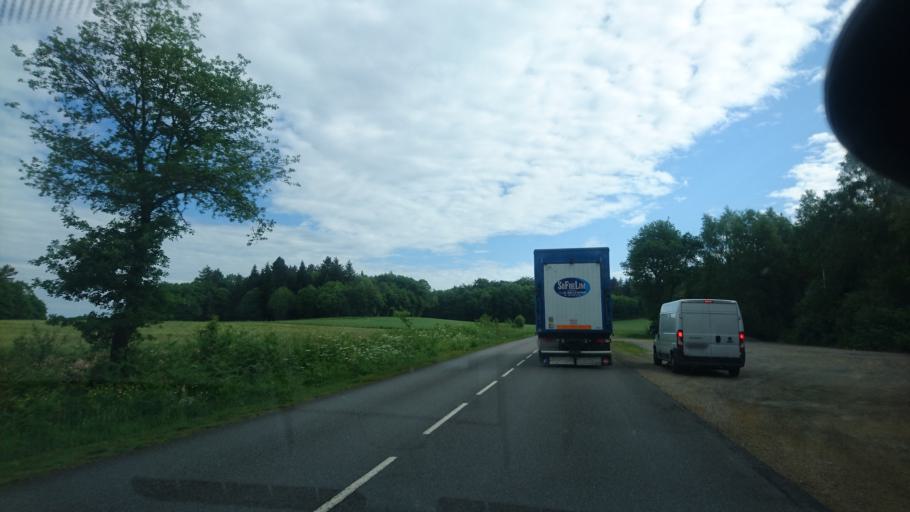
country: FR
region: Limousin
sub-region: Departement de la Haute-Vienne
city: Eymoutiers
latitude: 45.7656
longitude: 1.7507
